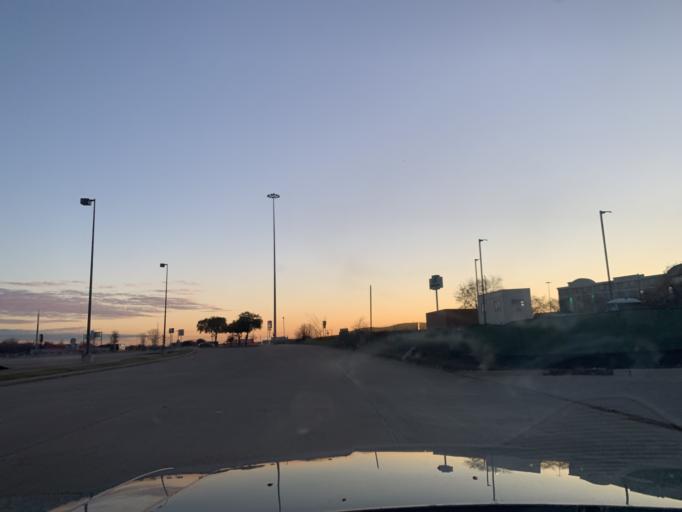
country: US
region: Texas
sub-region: Tarrant County
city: Bedford
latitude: 32.8401
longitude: -97.1163
